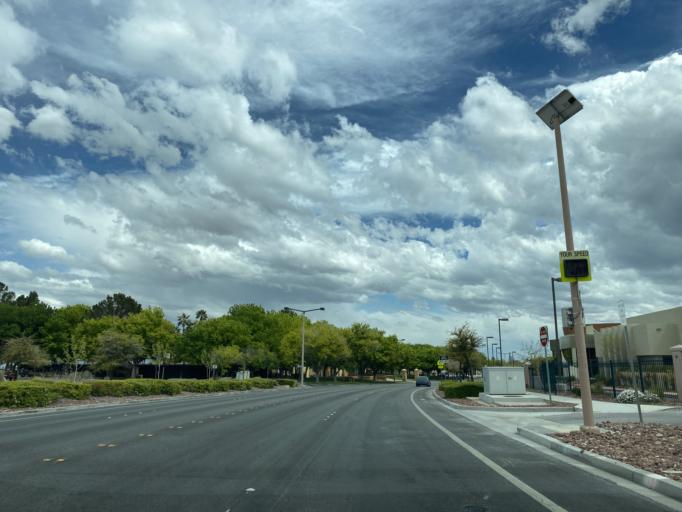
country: US
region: Nevada
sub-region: Clark County
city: Summerlin South
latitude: 36.1995
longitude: -115.2940
